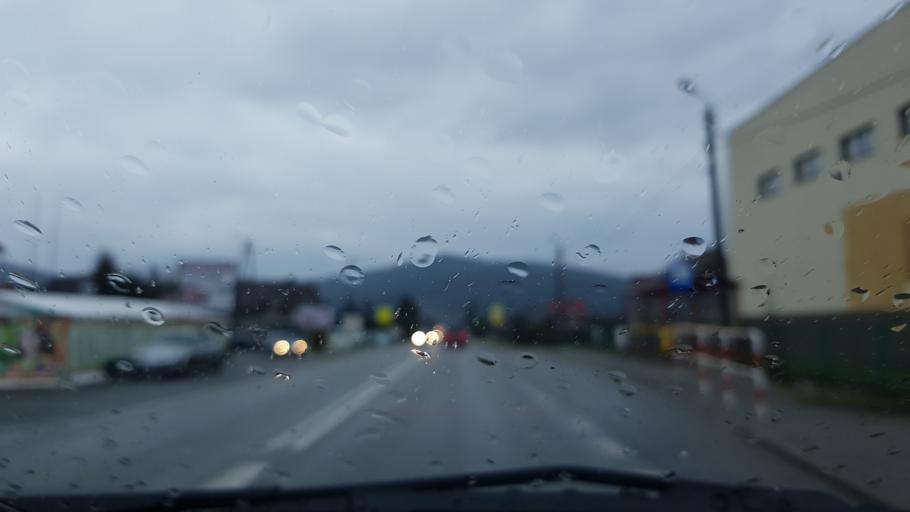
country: PL
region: Lesser Poland Voivodeship
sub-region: Powiat suski
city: Stryszawa
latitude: 49.7331
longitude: 19.5257
